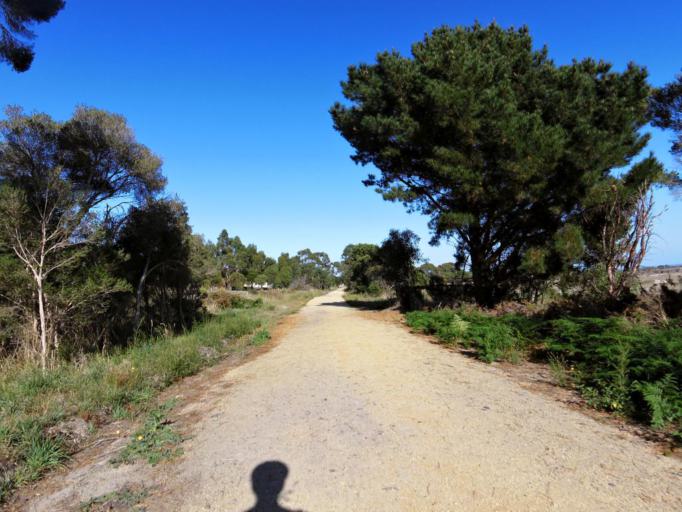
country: AU
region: Victoria
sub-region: Bass Coast
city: North Wonthaggi
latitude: -38.5032
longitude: 145.4981
